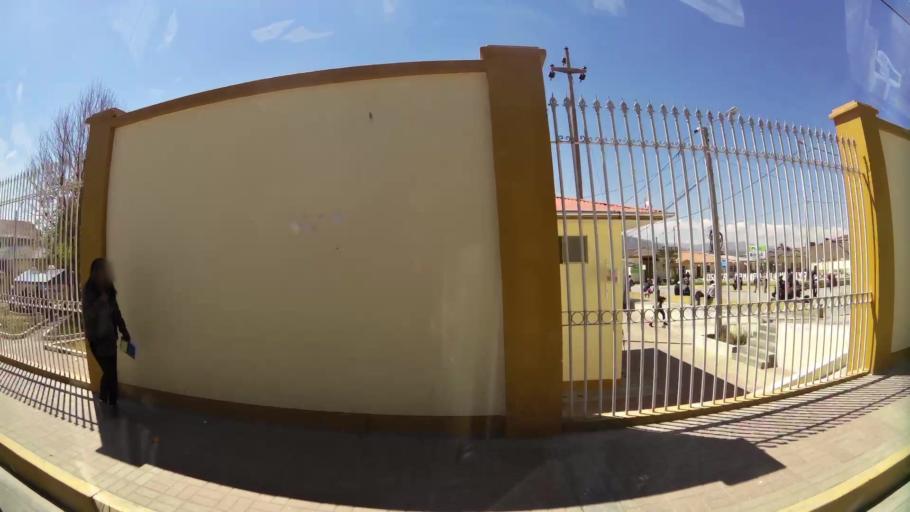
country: PE
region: Junin
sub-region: Provincia de Jauja
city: Jauja
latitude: -11.7771
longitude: -75.4969
